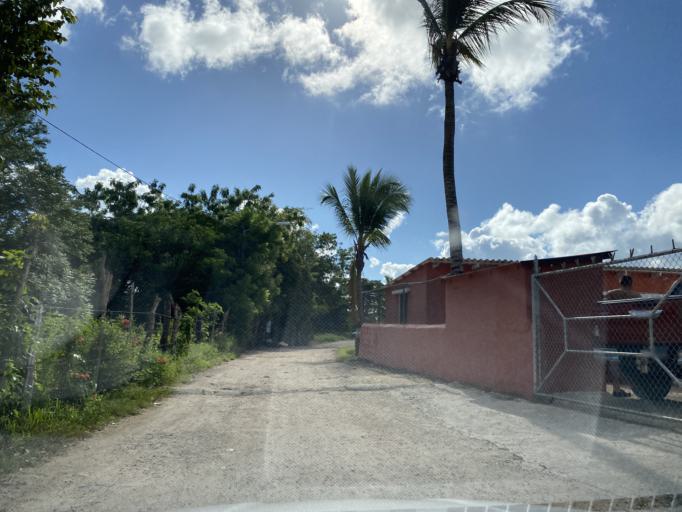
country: DO
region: La Romana
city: La Romana
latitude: 18.3648
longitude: -68.8415
